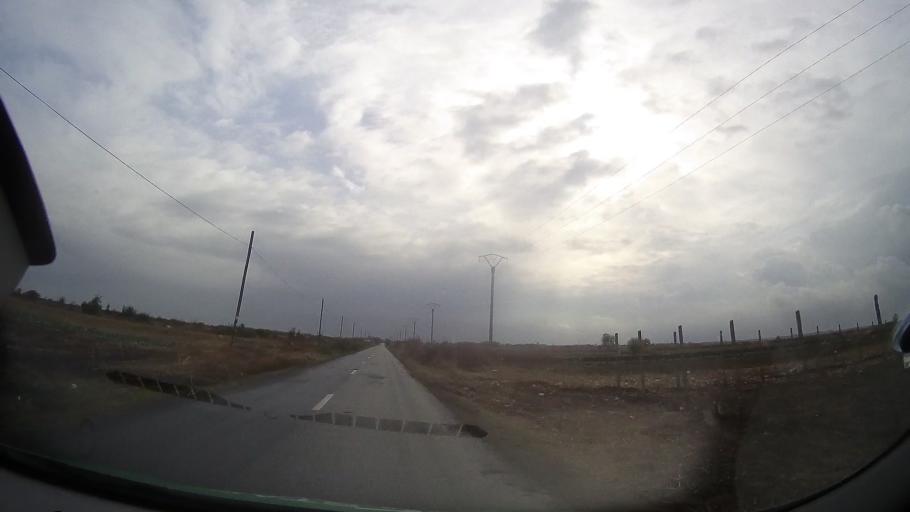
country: RO
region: Ialomita
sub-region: Comuna Fierbinti-Targ
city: Fierbintii de Jos
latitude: 44.7103
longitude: 26.3913
